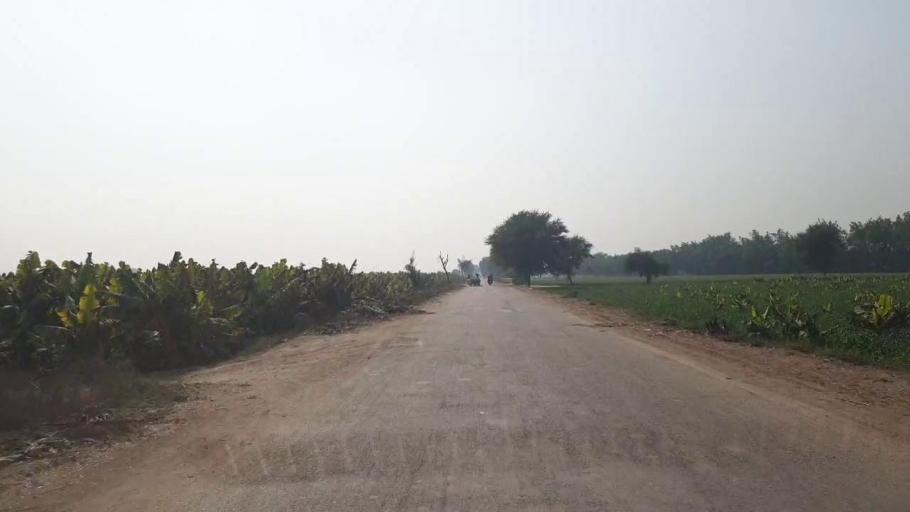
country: PK
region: Sindh
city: Hala
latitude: 25.8557
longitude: 68.4219
